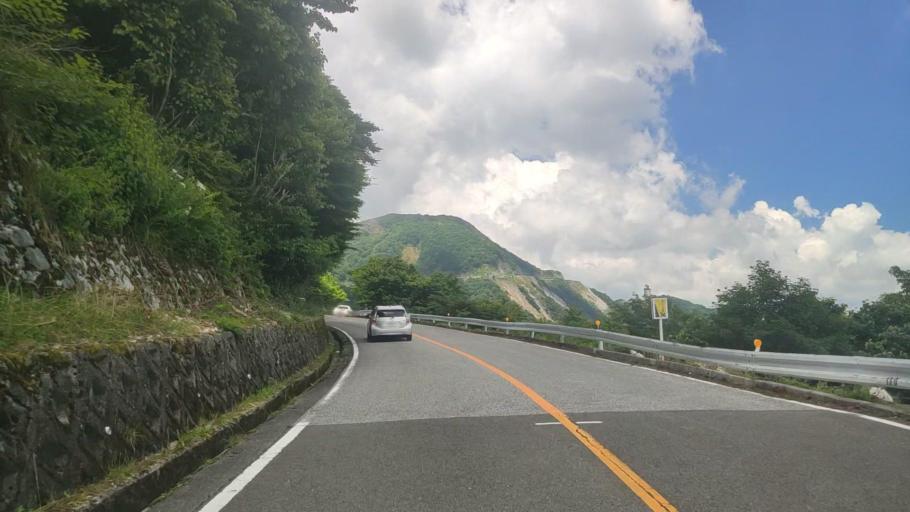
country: JP
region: Gifu
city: Tarui
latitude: 35.4153
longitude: 136.4209
